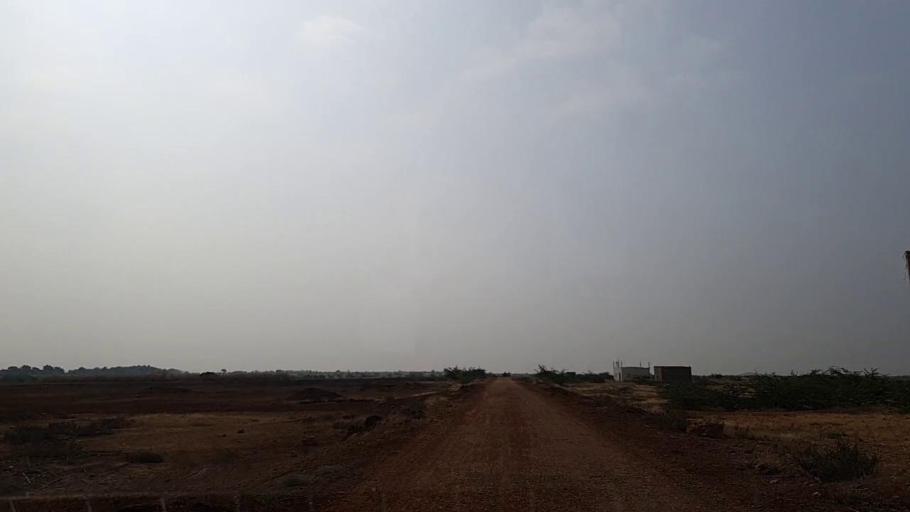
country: PK
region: Sindh
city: Thatta
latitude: 24.7378
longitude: 67.8395
